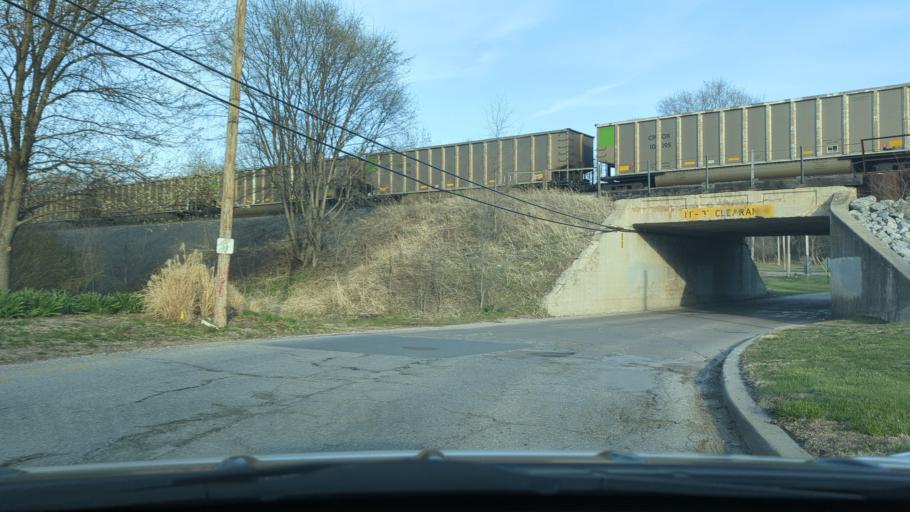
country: US
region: Nebraska
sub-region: Saunders County
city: Ashland
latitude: 41.0392
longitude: -96.3589
